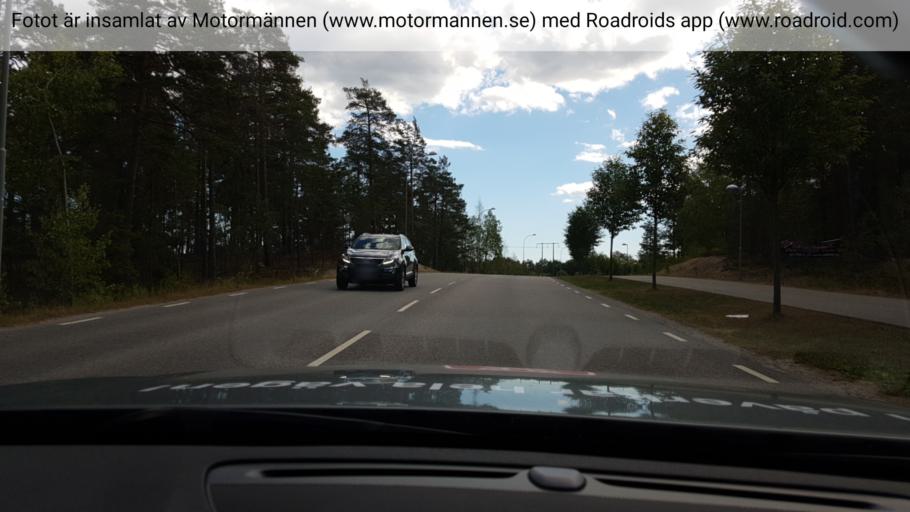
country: SE
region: Stockholm
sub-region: Nacka Kommun
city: Alta
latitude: 59.2454
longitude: 18.1944
